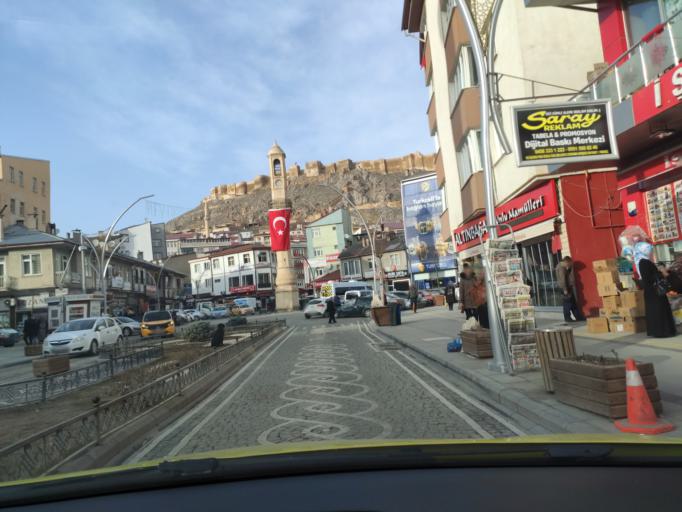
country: TR
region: Bayburt
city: Bayburt
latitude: 40.2599
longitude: 40.2270
